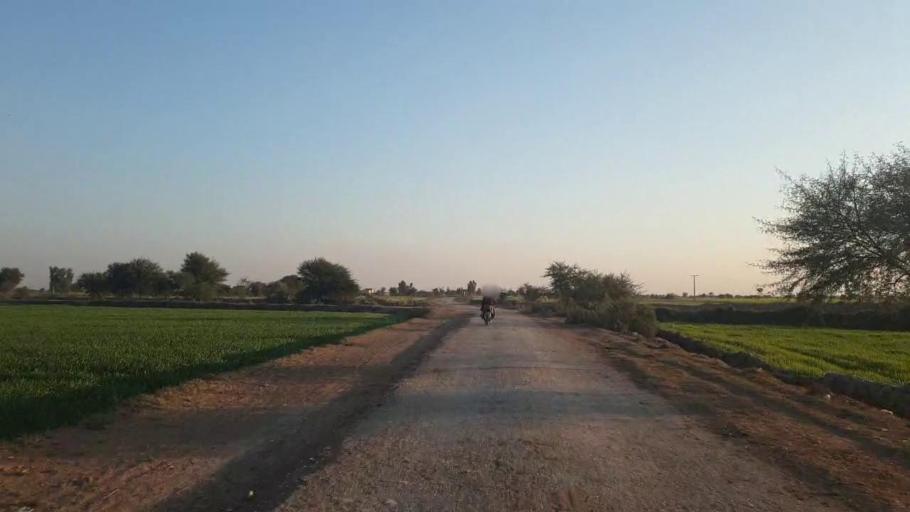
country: PK
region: Sindh
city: Khadro
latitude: 26.0791
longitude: 68.6990
